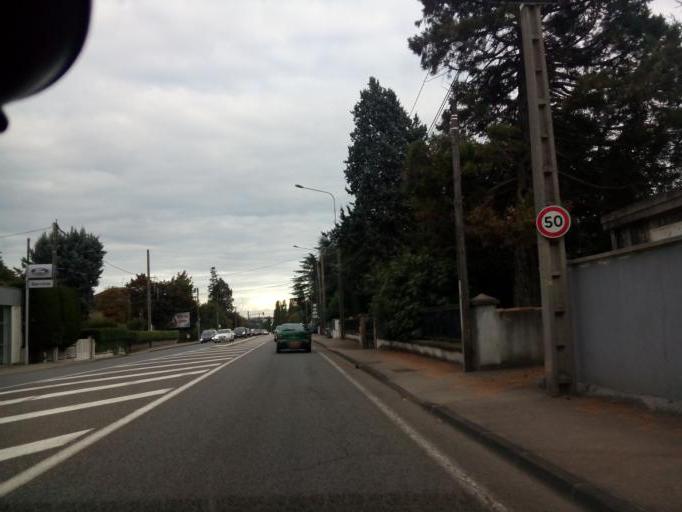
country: FR
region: Rhone-Alpes
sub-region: Departement du Rhone
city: Ecully
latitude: 45.7682
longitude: 4.7597
